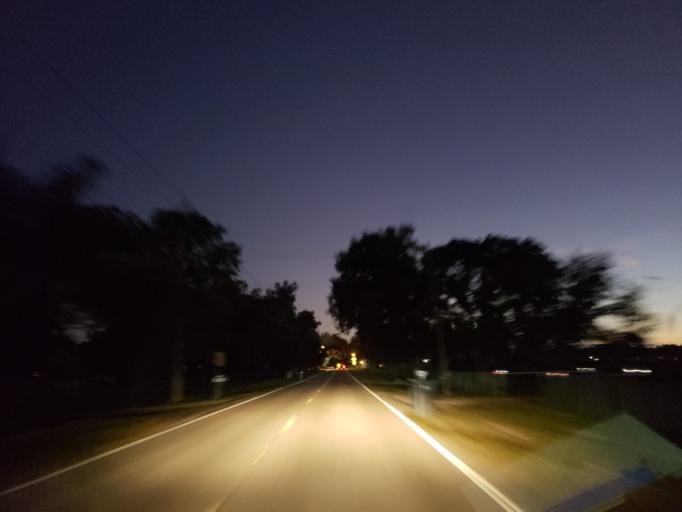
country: US
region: Florida
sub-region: Hillsborough County
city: Dover
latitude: 28.0101
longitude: -82.2241
